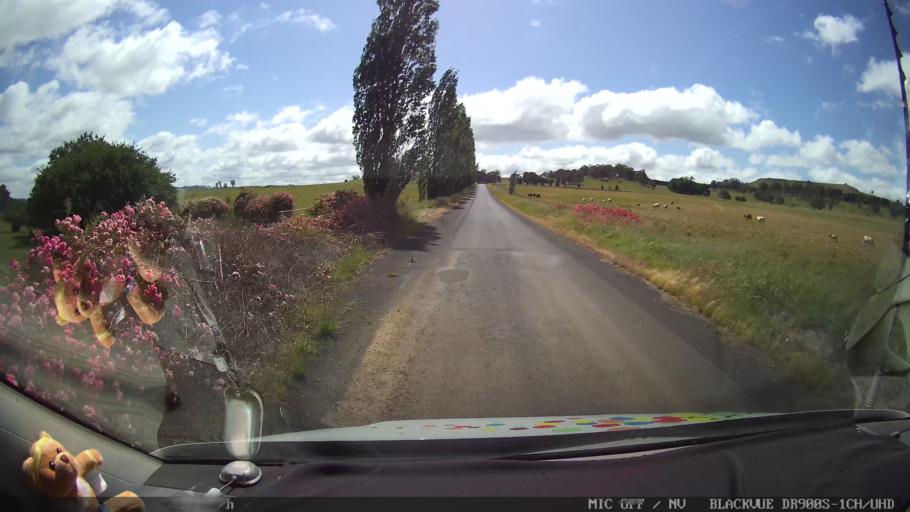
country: AU
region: New South Wales
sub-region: Glen Innes Severn
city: Glen Innes
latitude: -29.9446
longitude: 151.7161
